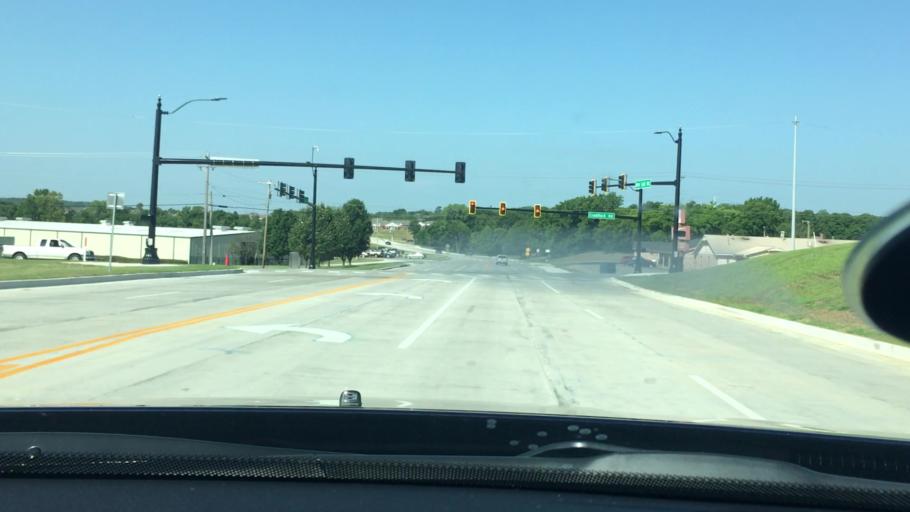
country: US
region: Oklahoma
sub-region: Pontotoc County
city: Ada
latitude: 34.7626
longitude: -96.6634
